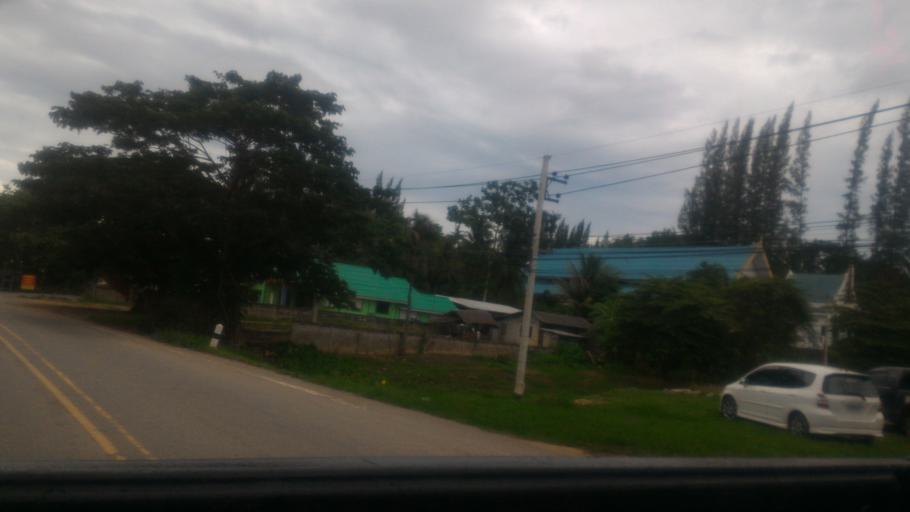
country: TH
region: Prachuap Khiri Khan
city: Kui Buri
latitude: 12.1063
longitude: 99.7544
